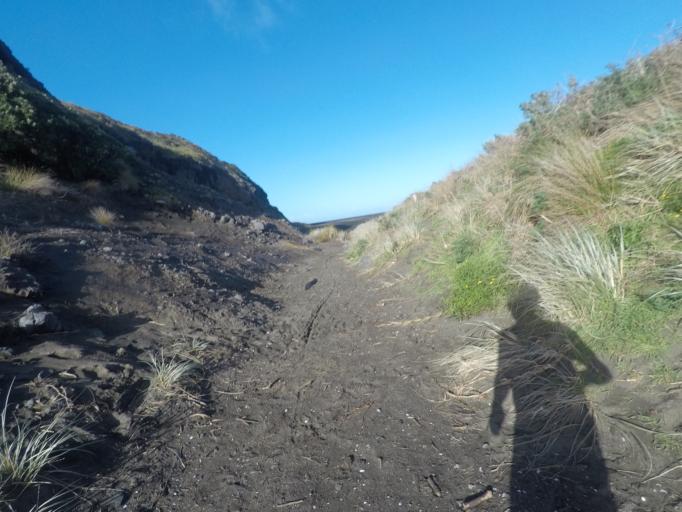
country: NZ
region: Auckland
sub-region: Auckland
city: Muriwai Beach
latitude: -36.9906
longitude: 174.4750
